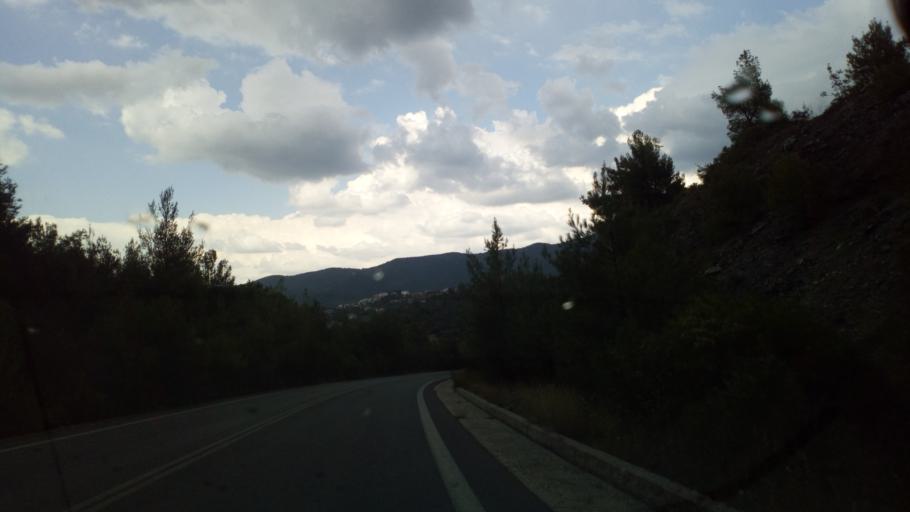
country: GR
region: Central Macedonia
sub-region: Nomos Chalkidikis
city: Polygyros
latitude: 40.3612
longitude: 23.4394
